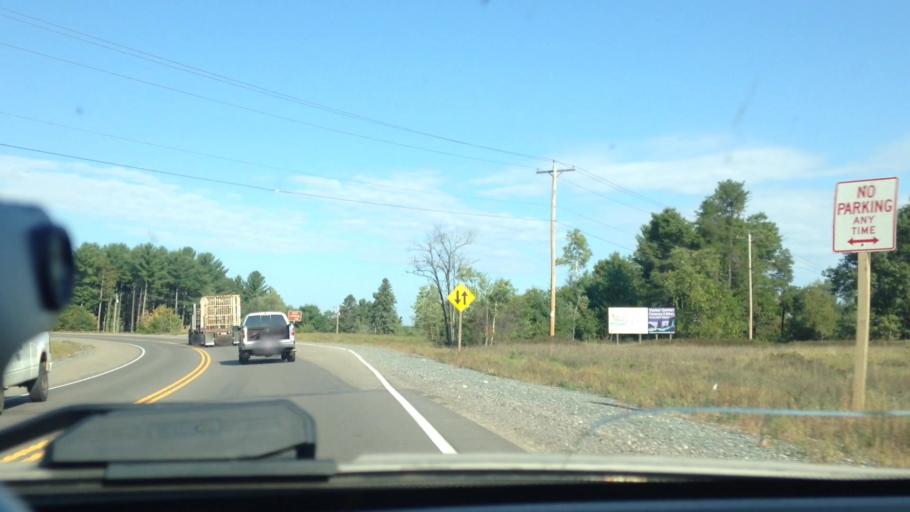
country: US
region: Michigan
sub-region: Dickinson County
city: Iron Mountain
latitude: 45.8746
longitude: -88.0855
